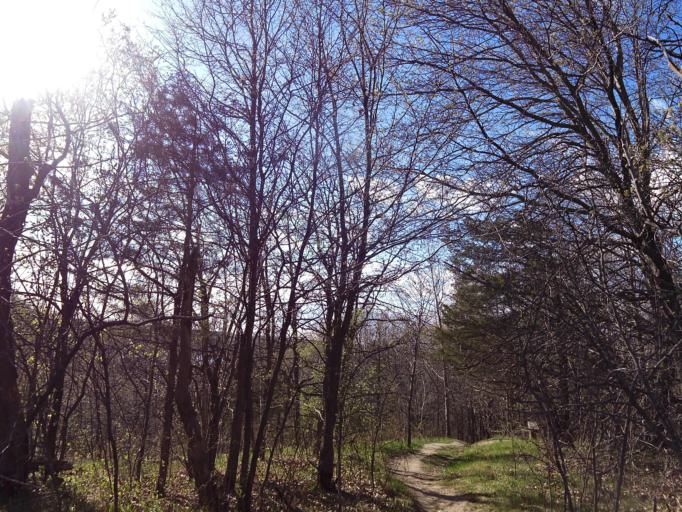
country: US
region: Wisconsin
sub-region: Saint Croix County
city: North Hudson
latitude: 45.0170
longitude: -92.6780
